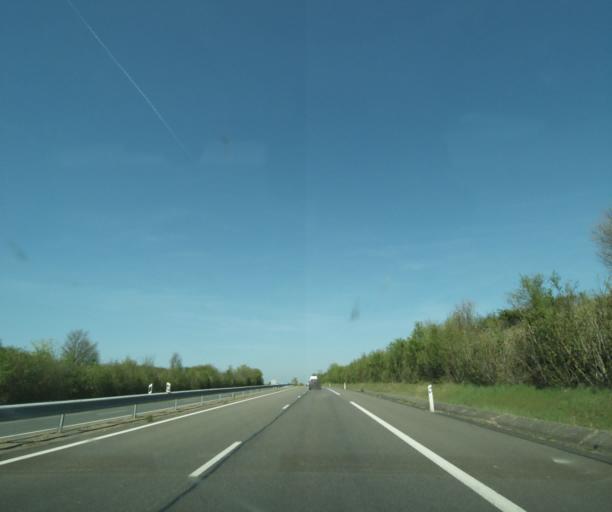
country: FR
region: Bourgogne
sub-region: Departement de la Nievre
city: La Charite-sur-Loire
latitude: 47.1706
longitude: 3.0486
